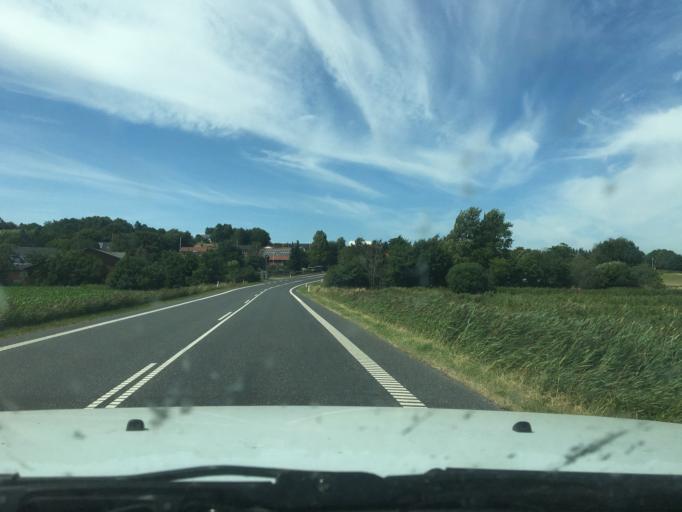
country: DK
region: Central Jutland
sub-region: Viborg Kommune
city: Viborg
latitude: 56.5739
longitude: 9.3788
